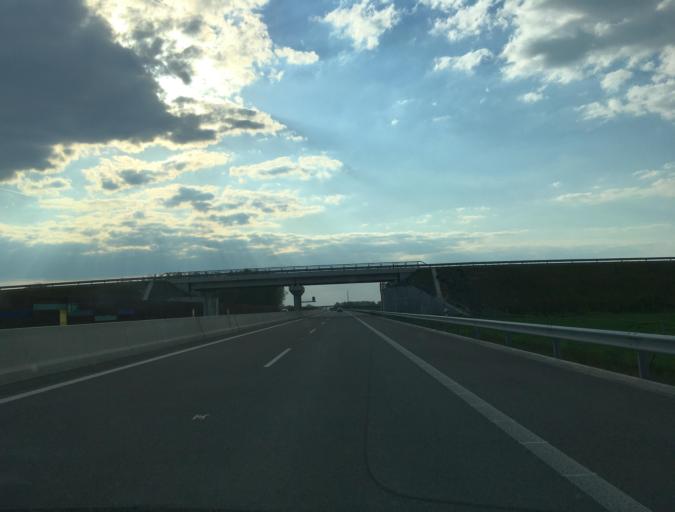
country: SK
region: Trnavsky
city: Samorin
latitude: 48.0142
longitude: 17.4455
